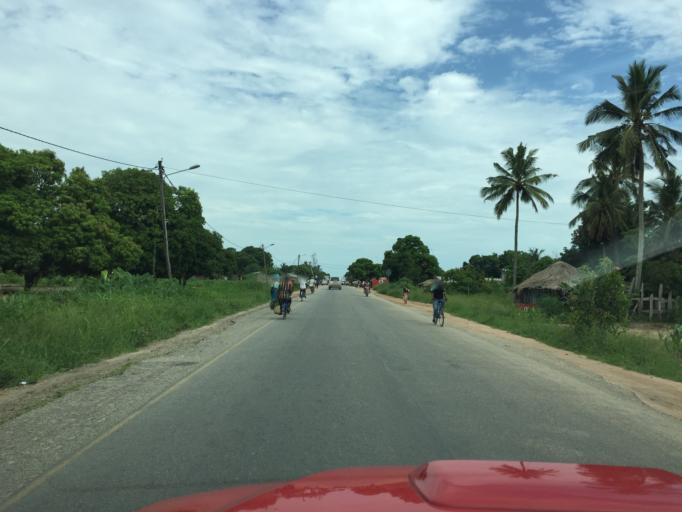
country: MZ
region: Zambezia
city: Quelimane
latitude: -17.5974
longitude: 36.8166
